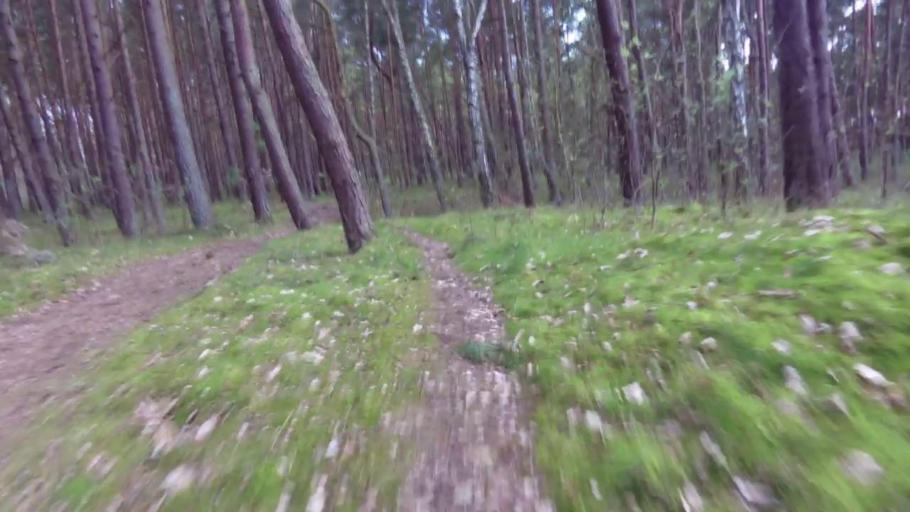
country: PL
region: West Pomeranian Voivodeship
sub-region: Powiat kamienski
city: Dziwnow
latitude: 53.9986
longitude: 14.6532
